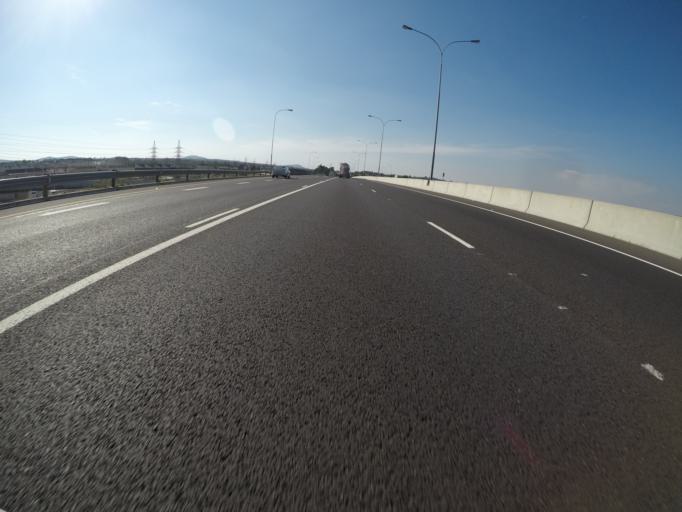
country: ZA
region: Western Cape
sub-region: City of Cape Town
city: Kraaifontein
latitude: -33.8913
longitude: 18.6767
